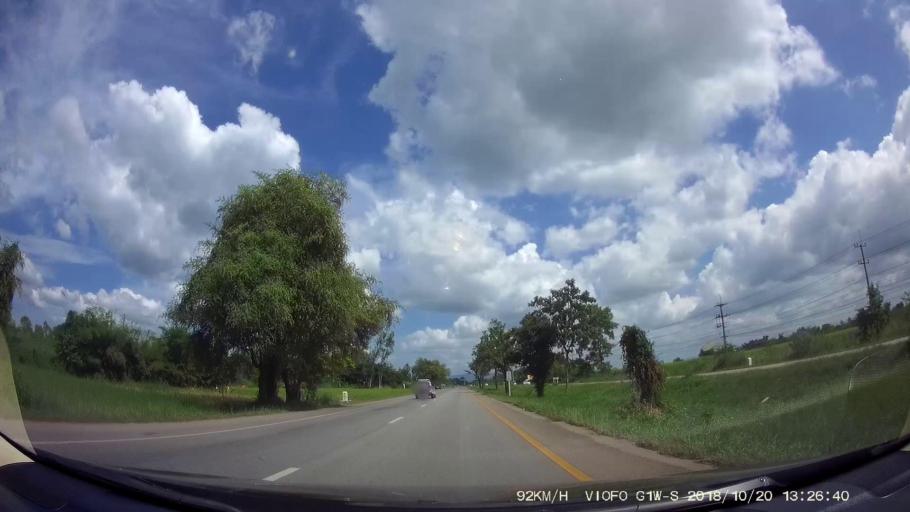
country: TH
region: Chaiyaphum
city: Khon San
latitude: 16.5935
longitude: 101.9496
